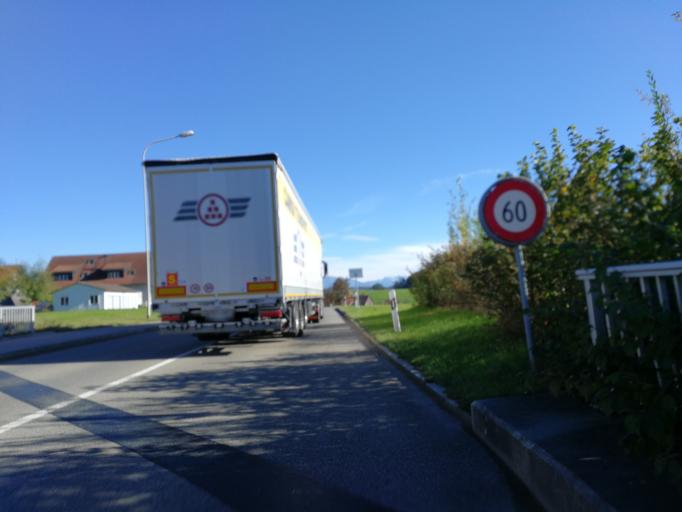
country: CH
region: Zurich
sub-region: Bezirk Hinwil
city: Binzikon
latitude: 47.2879
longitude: 8.7404
